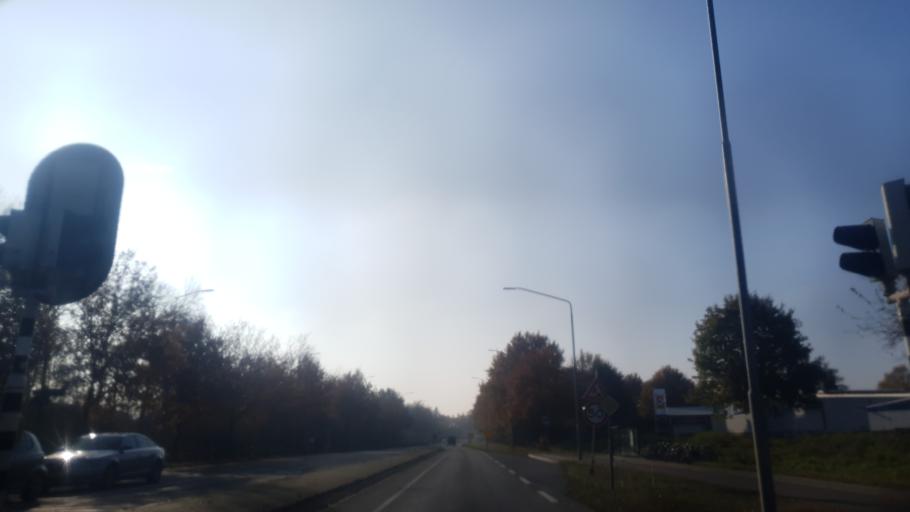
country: NL
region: North Brabant
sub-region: Gemeente Grave
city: Grave
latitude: 51.7542
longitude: 5.7346
